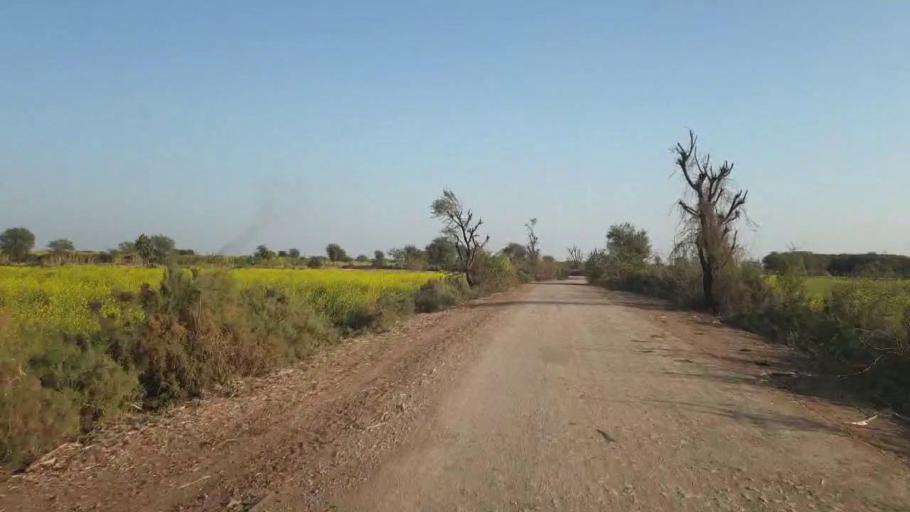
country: PK
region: Sindh
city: Tando Allahyar
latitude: 25.3747
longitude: 68.7070
